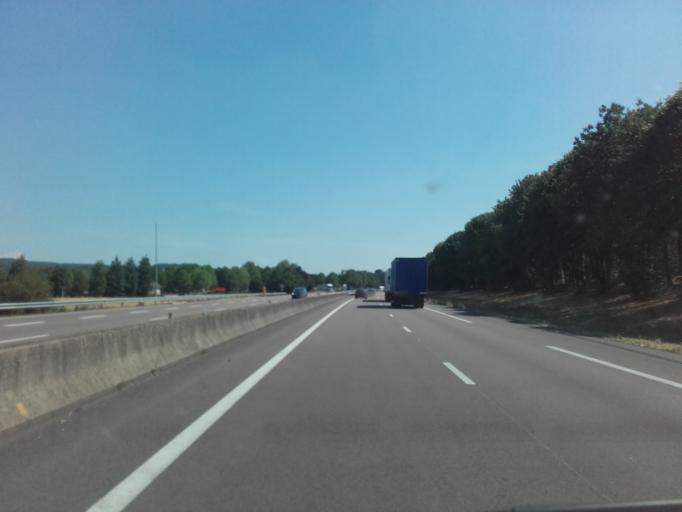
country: FR
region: Bourgogne
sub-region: Departement de la Cote-d'Or
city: Pouilly-en-Auxois
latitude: 47.3143
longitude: 4.4976
